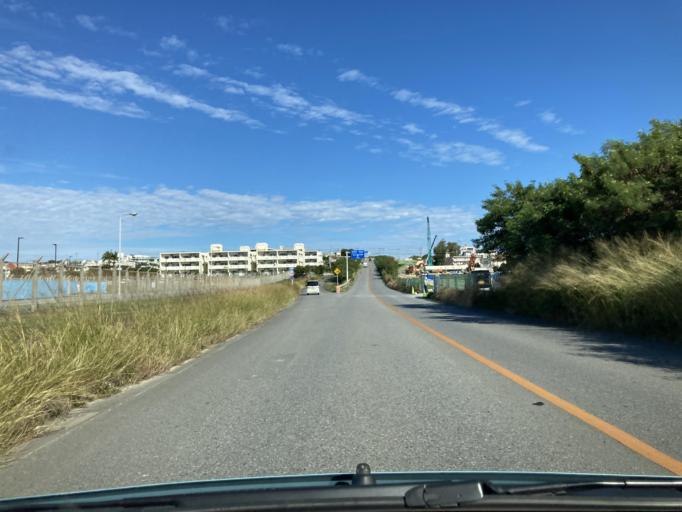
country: JP
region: Okinawa
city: Okinawa
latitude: 26.3779
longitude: 127.7455
